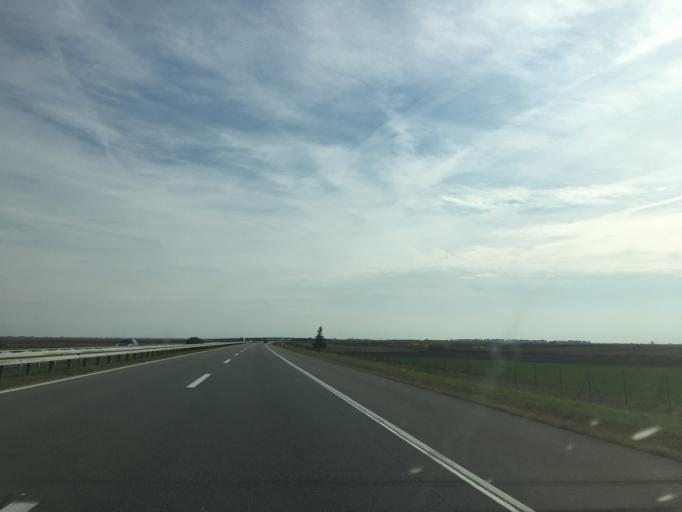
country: RS
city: Novi Karlovci
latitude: 45.0564
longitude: 20.1680
